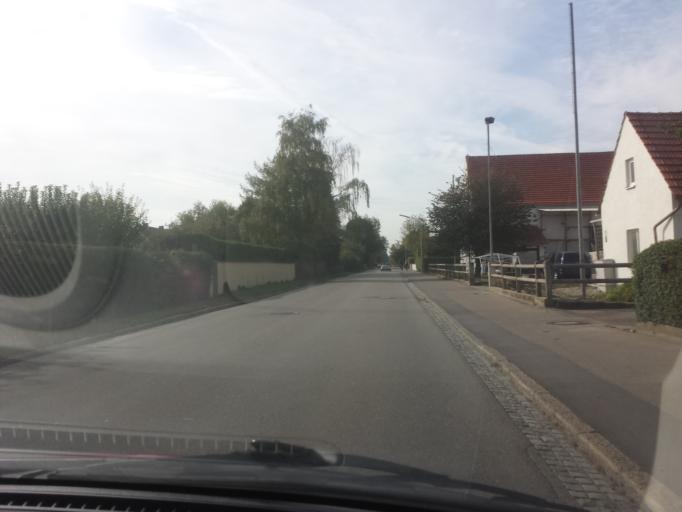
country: DE
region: Bavaria
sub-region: Upper Bavaria
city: Bergheim
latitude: 48.7372
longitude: 11.2313
